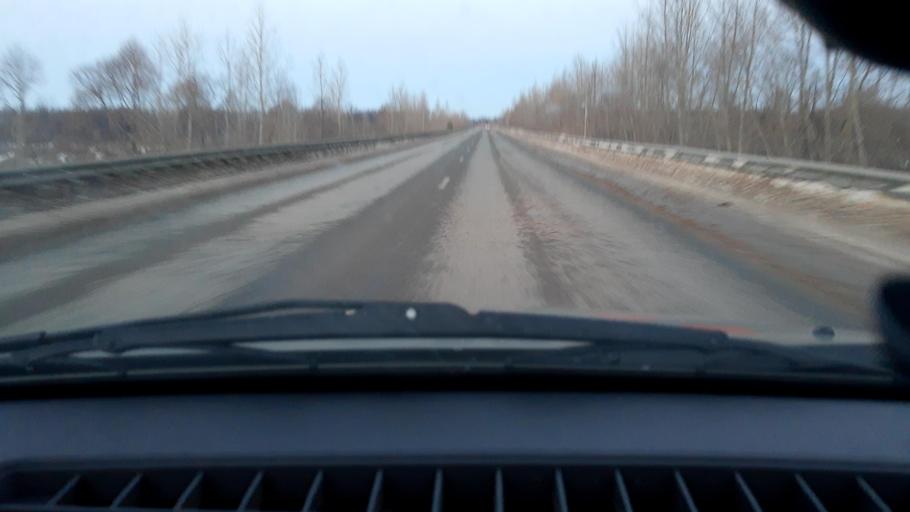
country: RU
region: Bashkortostan
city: Blagoveshchensk
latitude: 55.0215
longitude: 55.7897
